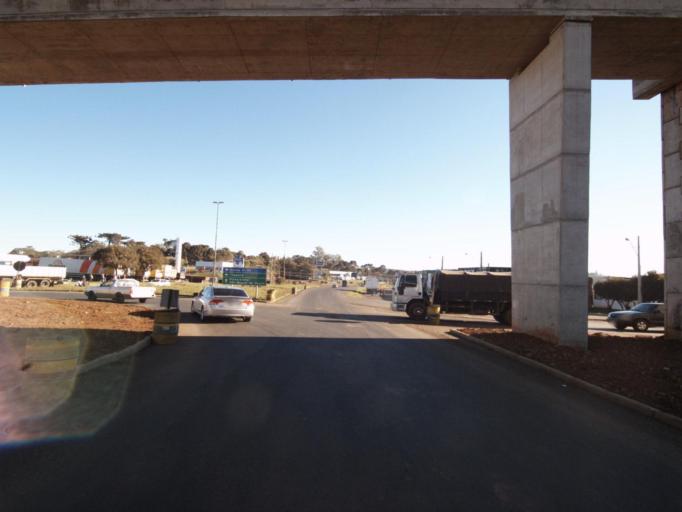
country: BR
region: Santa Catarina
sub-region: Chapeco
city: Chapeco
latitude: -26.9993
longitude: -52.6464
